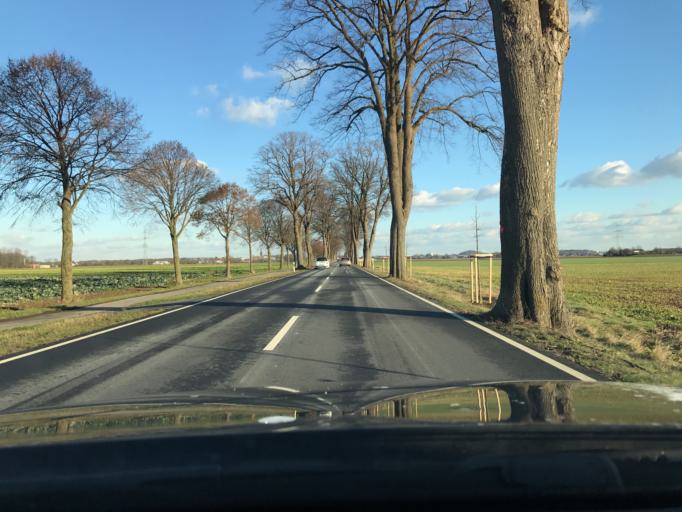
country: DE
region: North Rhine-Westphalia
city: Tonisvorst
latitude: 51.3648
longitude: 6.4789
